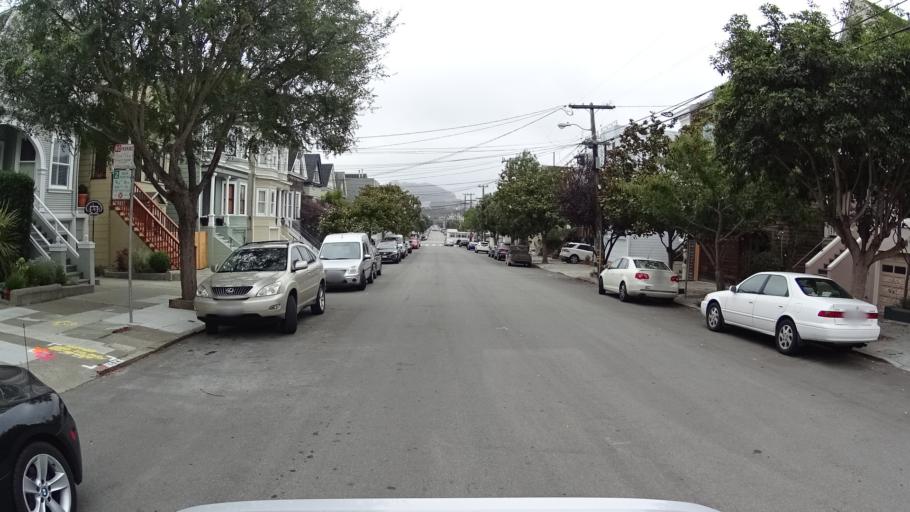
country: US
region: California
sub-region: San Francisco County
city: San Francisco
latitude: 37.7866
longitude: -122.4615
